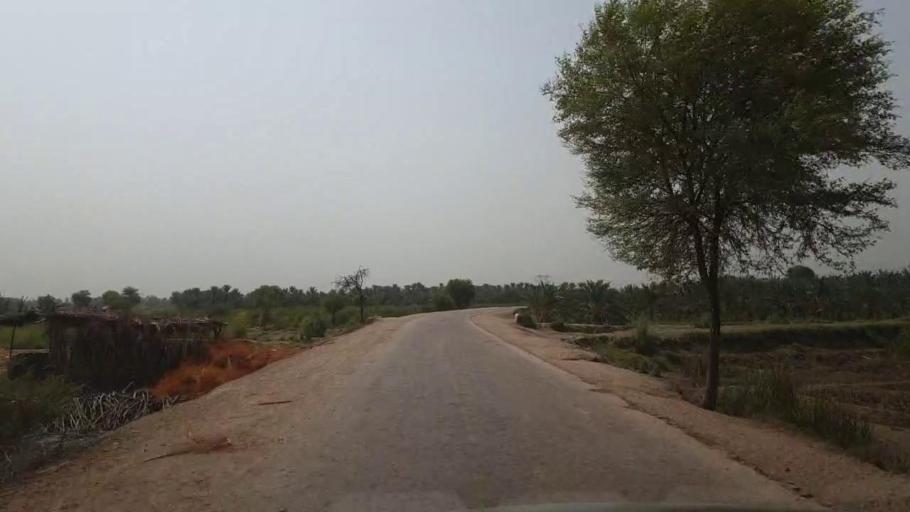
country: PK
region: Sindh
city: Gambat
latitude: 27.4196
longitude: 68.5475
